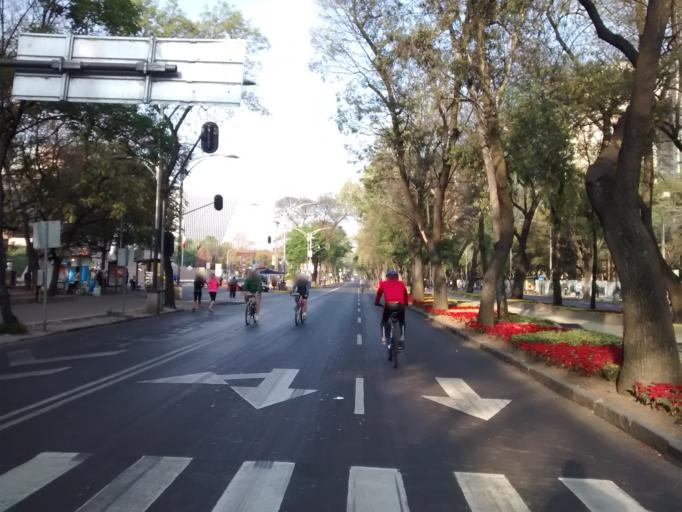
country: MX
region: Mexico City
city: Polanco
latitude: 19.4259
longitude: -99.1929
